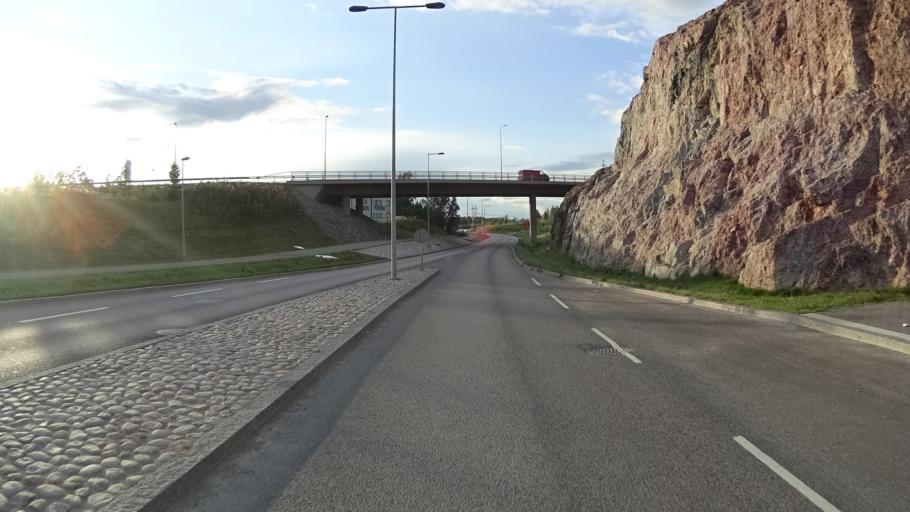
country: FI
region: Uusimaa
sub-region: Helsinki
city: Teekkarikylae
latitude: 60.3091
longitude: 24.8915
